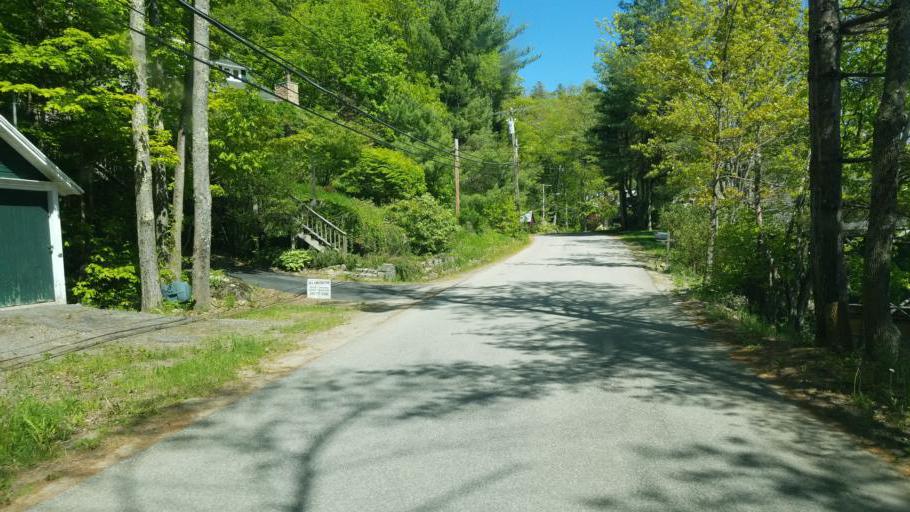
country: US
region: New York
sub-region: Fulton County
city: Gloversville
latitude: 43.1680
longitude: -74.5050
